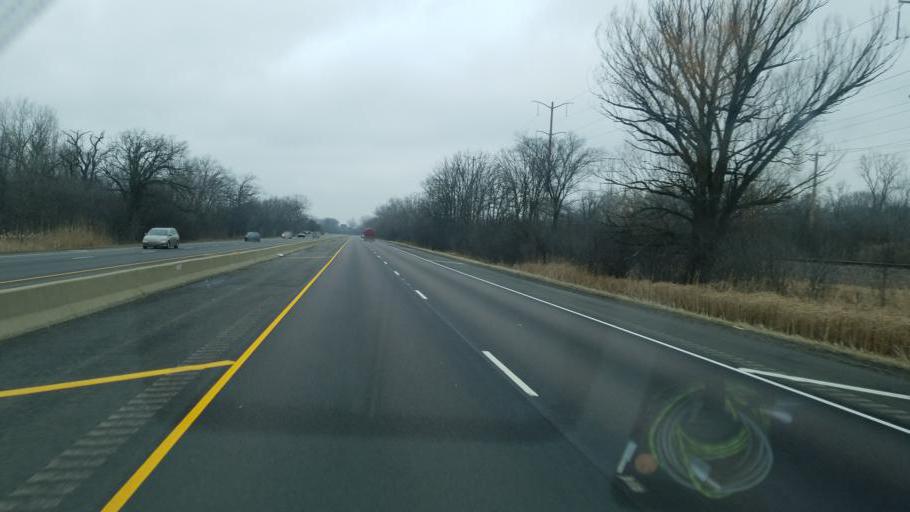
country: US
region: Illinois
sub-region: Lake County
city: Lake Forest
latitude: 42.2653
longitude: -87.8634
